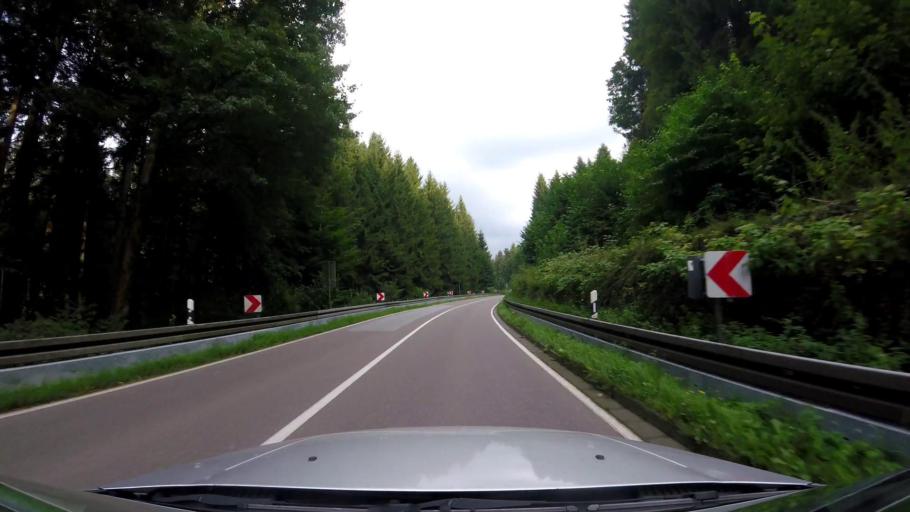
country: DE
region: Baden-Wuerttemberg
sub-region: Regierungsbezirk Stuttgart
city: Durlangen
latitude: 48.8475
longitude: 9.7772
